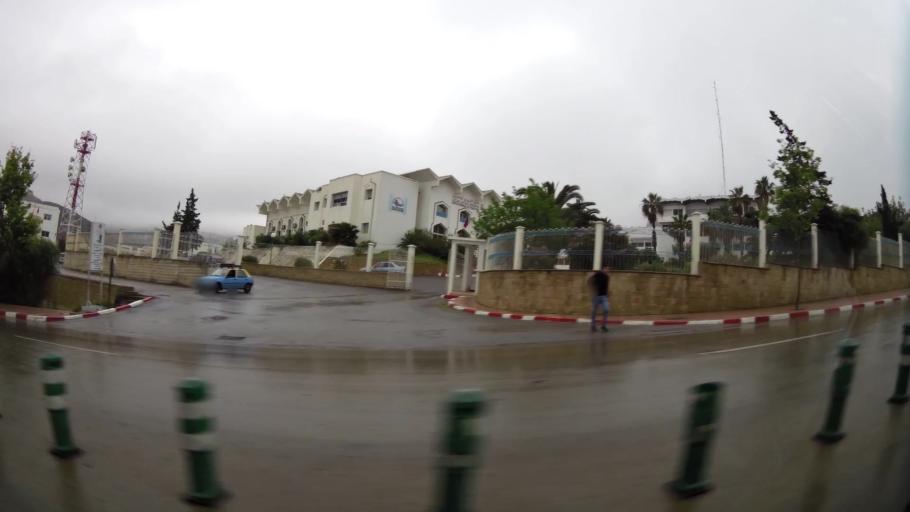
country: MA
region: Taza-Al Hoceima-Taounate
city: Al Hoceima
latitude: 35.2368
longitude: -3.9262
